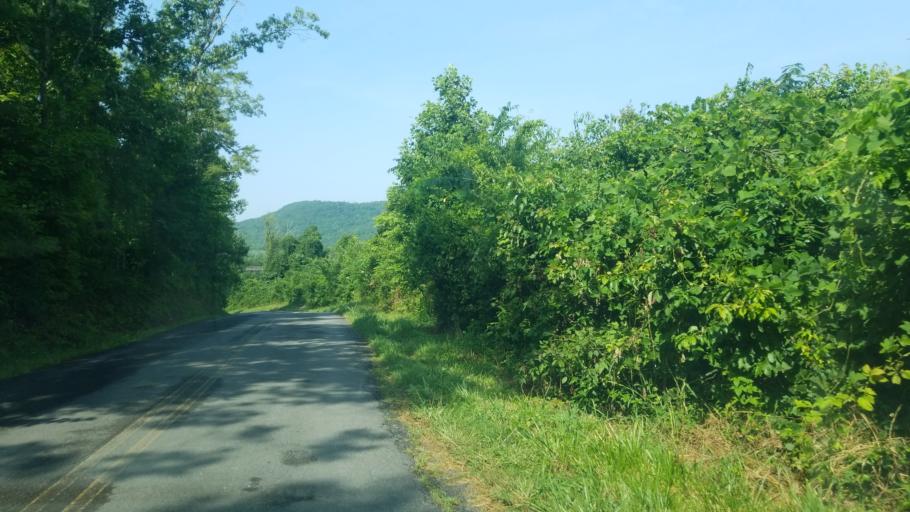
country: US
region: Tennessee
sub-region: Hamilton County
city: Collegedale
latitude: 35.0837
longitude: -84.9927
